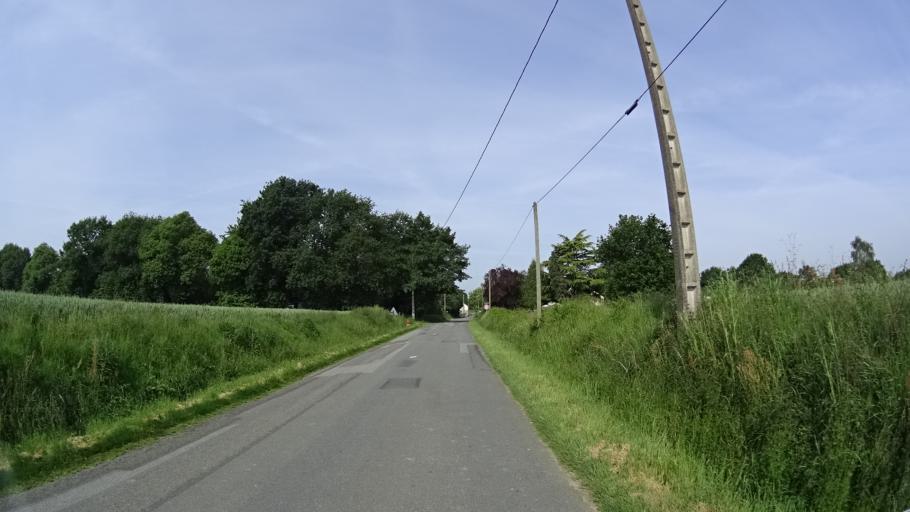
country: FR
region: Brittany
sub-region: Departement d'Ille-et-Vilaine
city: Chateaugiron
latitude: 48.0357
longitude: -1.5182
